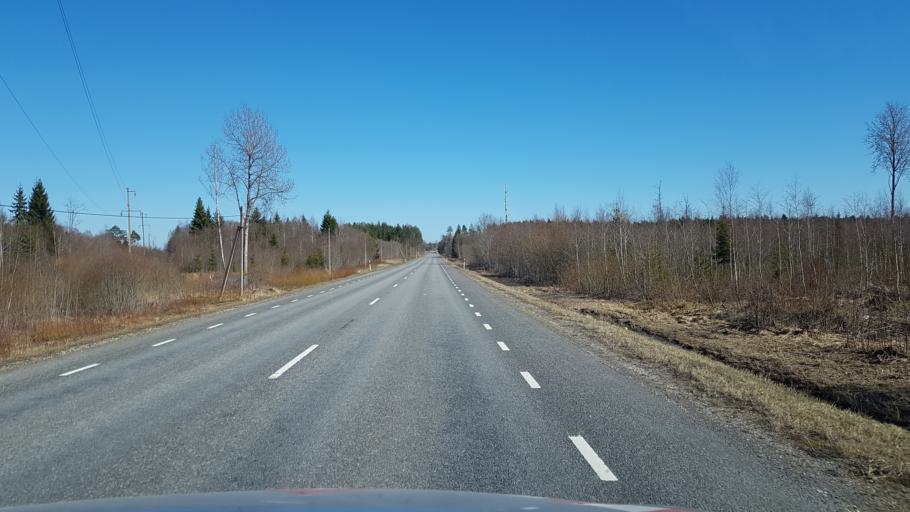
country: EE
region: Ida-Virumaa
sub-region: Aseri vald
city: Aseri
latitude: 59.3532
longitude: 26.7396
